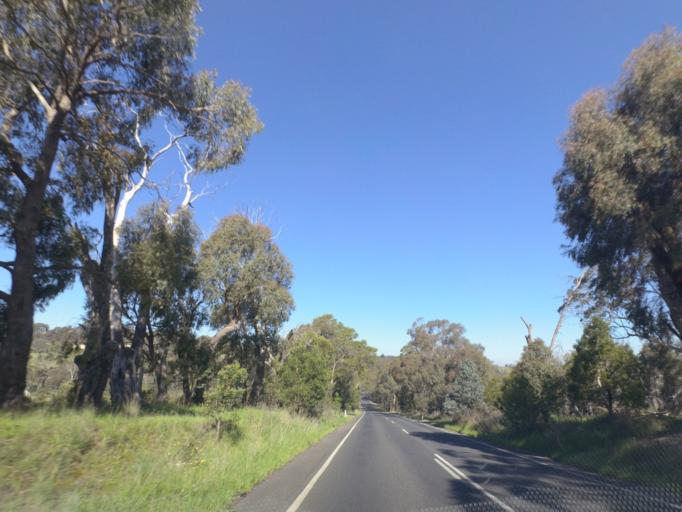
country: AU
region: Victoria
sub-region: Whittlesea
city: Whittlesea
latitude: -37.3403
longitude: 144.9897
